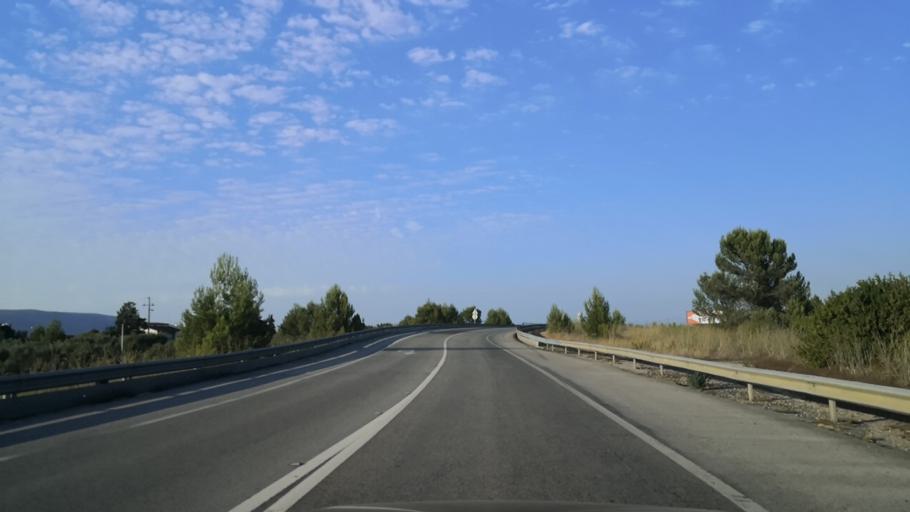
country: PT
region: Santarem
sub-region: Alcanena
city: Alcanena
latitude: 39.4332
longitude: -8.6293
